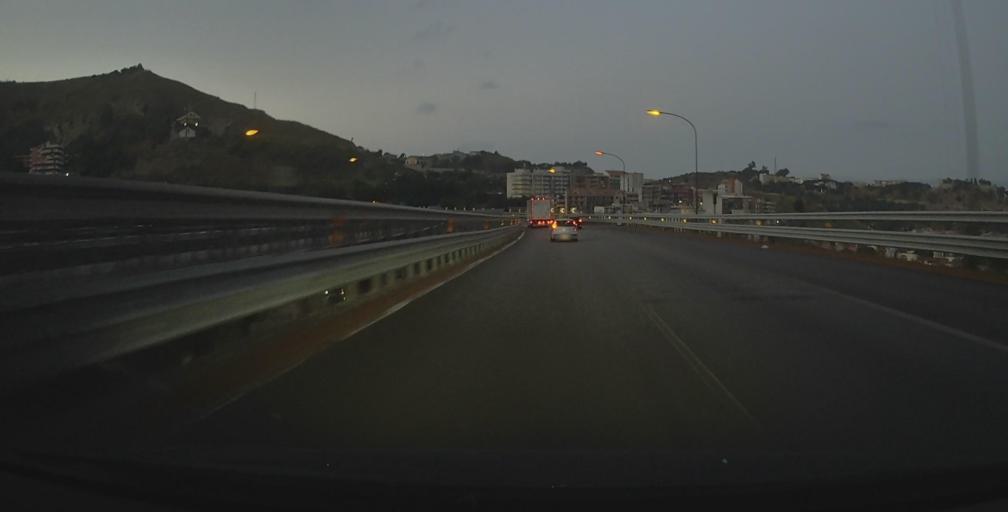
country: IT
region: Sicily
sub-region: Messina
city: Messina
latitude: 38.1872
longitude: 15.5273
